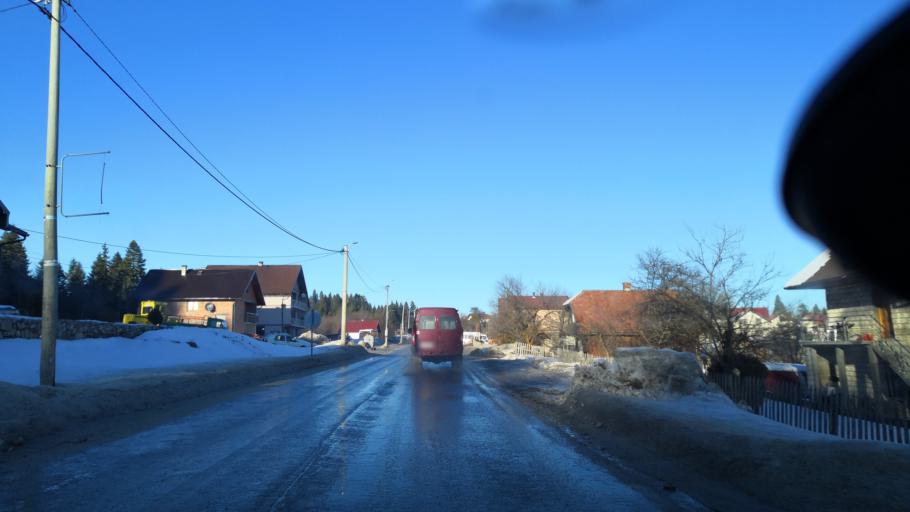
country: BA
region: Republika Srpska
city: Han Pijesak
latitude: 44.0696
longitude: 18.9459
